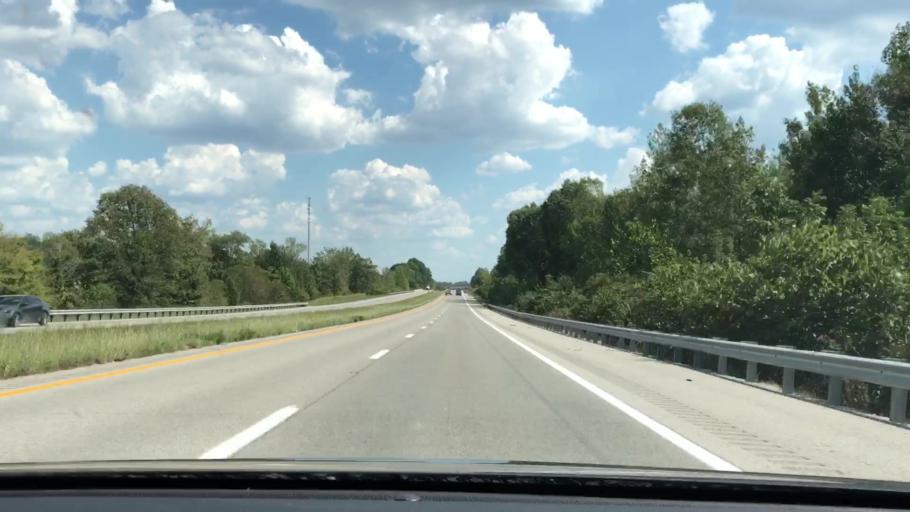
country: US
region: Kentucky
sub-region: Hopkins County
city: Dawson Springs
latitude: 37.1925
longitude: -87.6242
